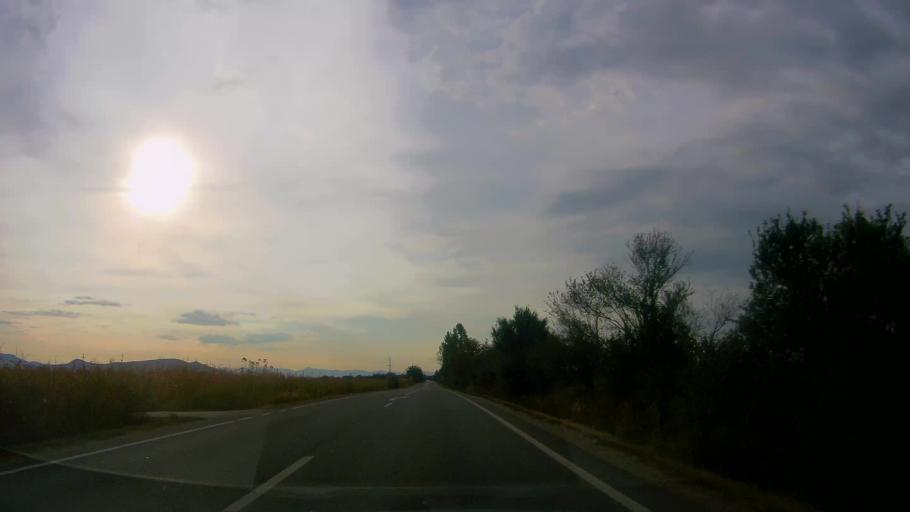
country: RO
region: Satu Mare
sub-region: Comuna Turulung
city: Turulung
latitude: 47.9508
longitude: 23.0660
